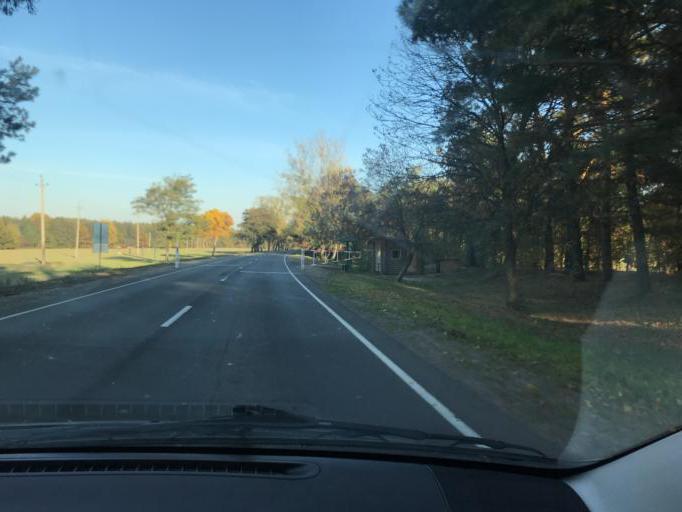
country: BY
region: Brest
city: Stolin
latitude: 51.8410
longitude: 26.7510
